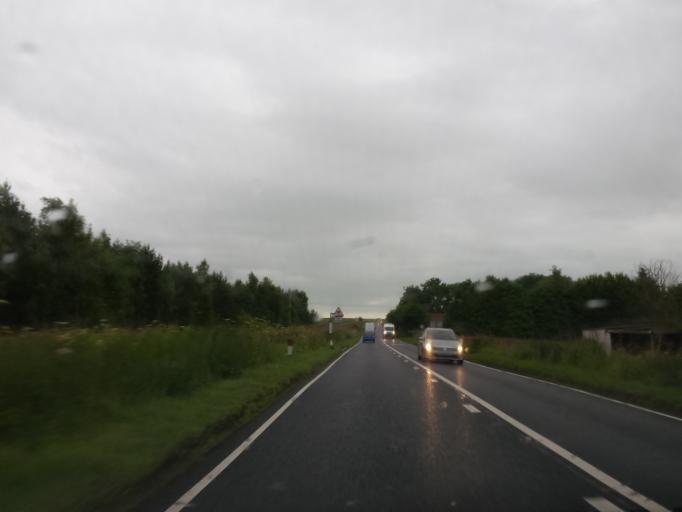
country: GB
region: Scotland
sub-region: Fife
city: Newport-On-Tay
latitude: 56.4113
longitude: -2.9146
